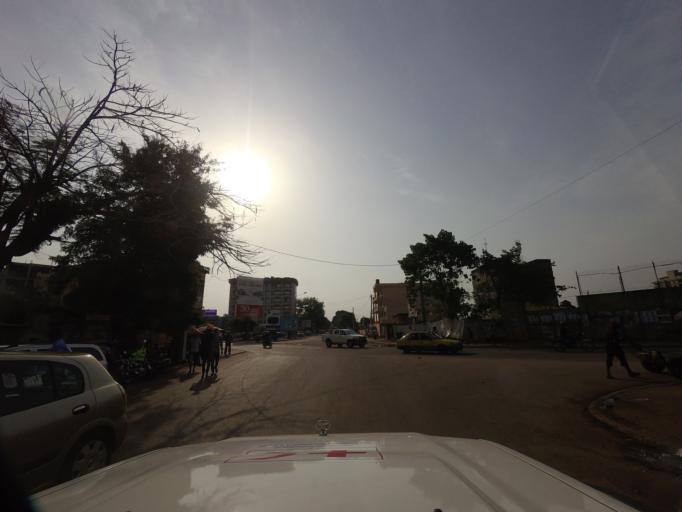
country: GN
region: Conakry
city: Camayenne
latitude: 9.5131
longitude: -13.7038
